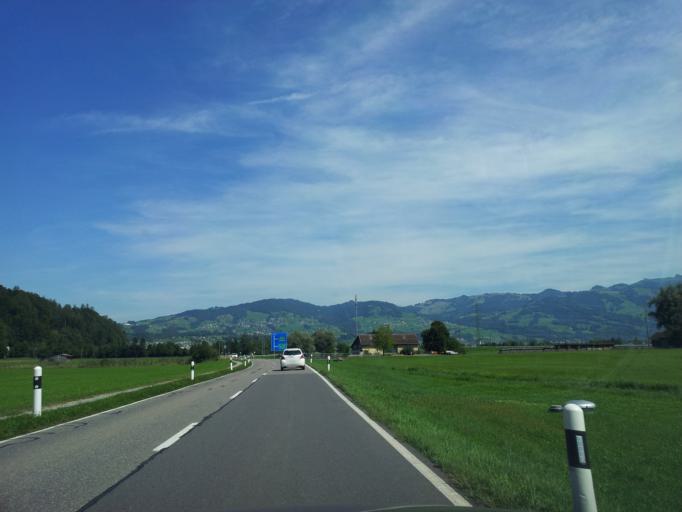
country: CH
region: Schwyz
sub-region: Bezirk March
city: Tuggen
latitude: 47.2074
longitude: 8.9562
